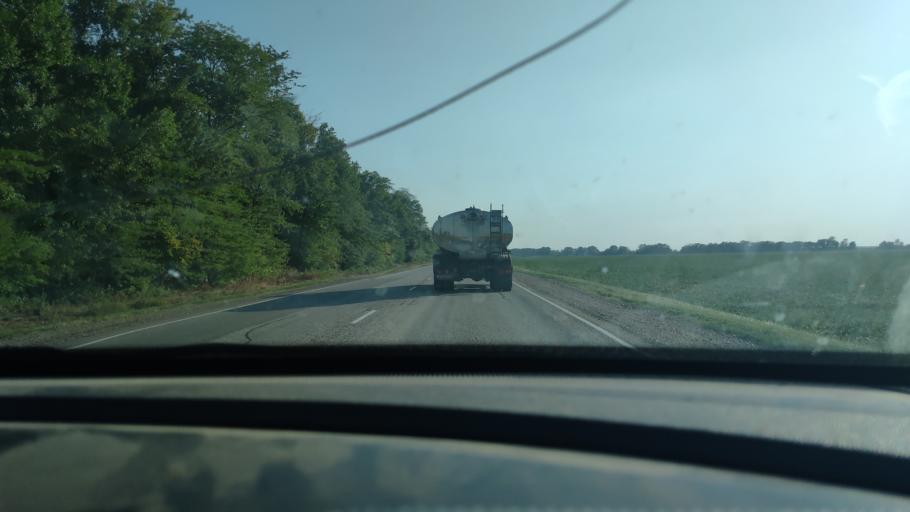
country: RU
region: Krasnodarskiy
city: Starominskaya
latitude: 46.4604
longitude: 39.0368
